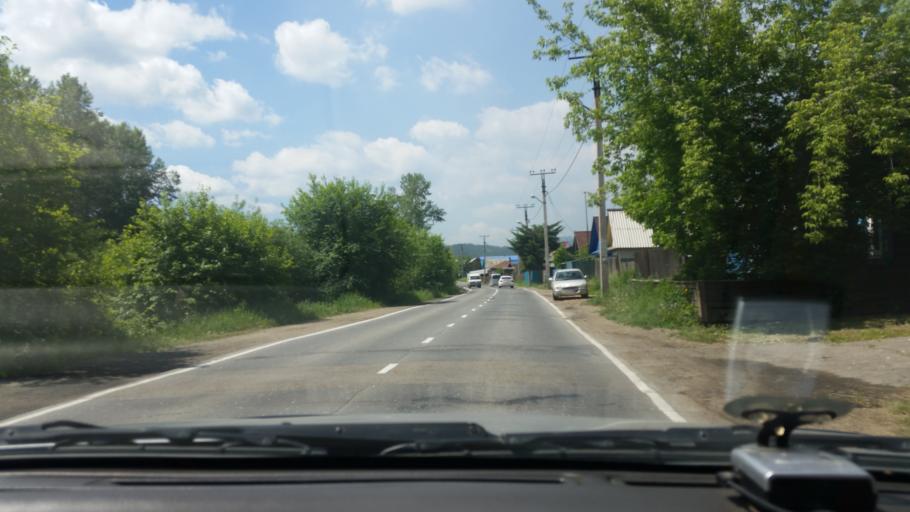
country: RU
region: Irkutsk
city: Shelekhov
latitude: 52.1608
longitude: 104.0914
